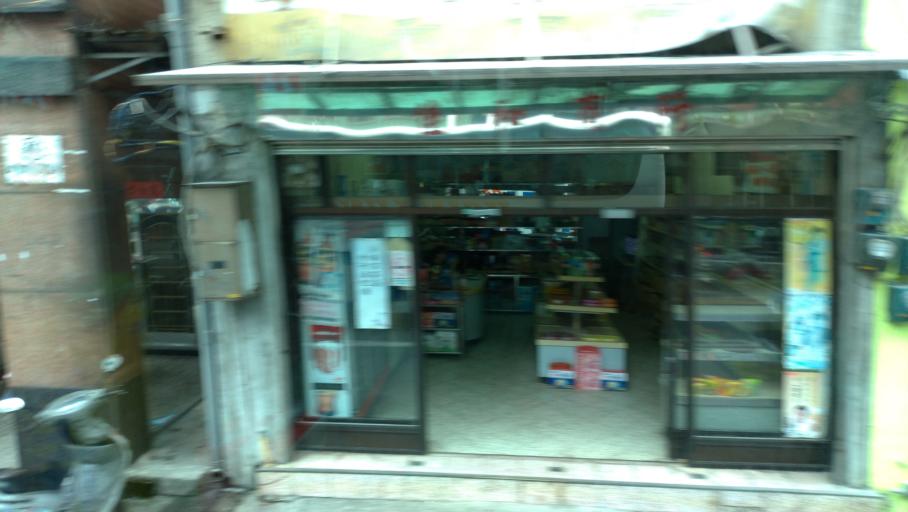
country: TW
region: Taiwan
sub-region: Keelung
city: Keelung
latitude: 25.1518
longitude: 121.7706
